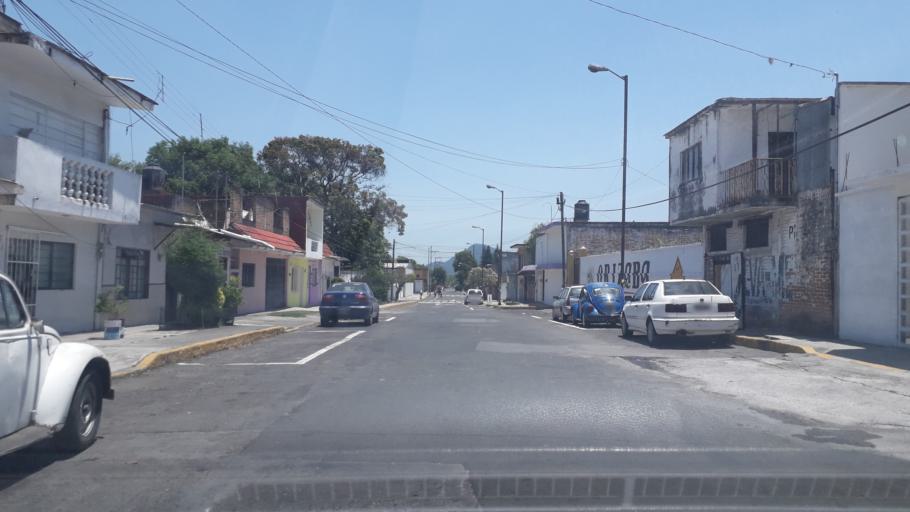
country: MX
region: Veracruz
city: Jalapilla
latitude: 18.8378
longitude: -97.0924
